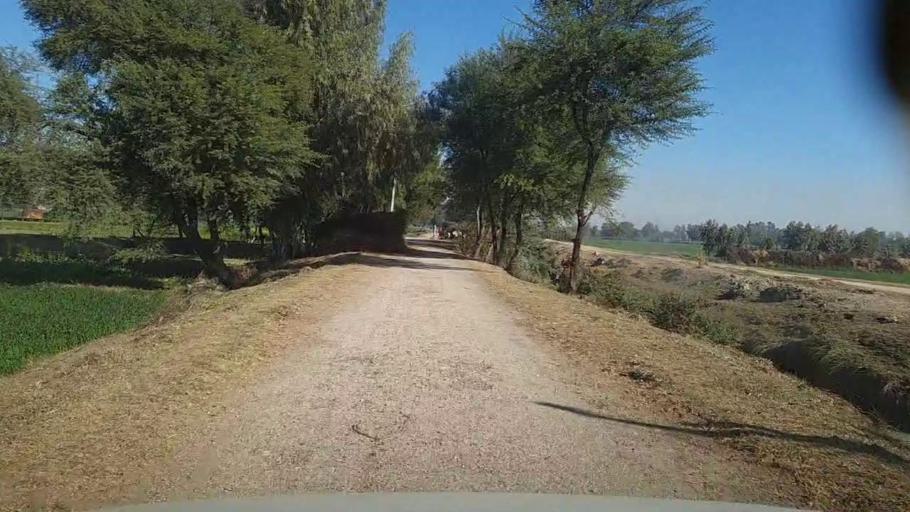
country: PK
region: Sindh
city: Khairpur
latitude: 28.0209
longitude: 69.6879
